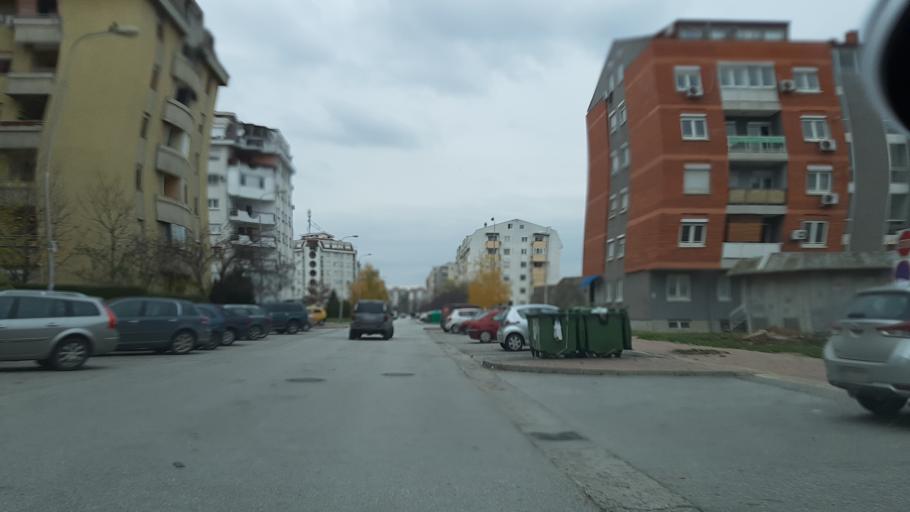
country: MK
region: Kisela Voda
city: Usje
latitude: 41.9788
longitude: 21.4758
